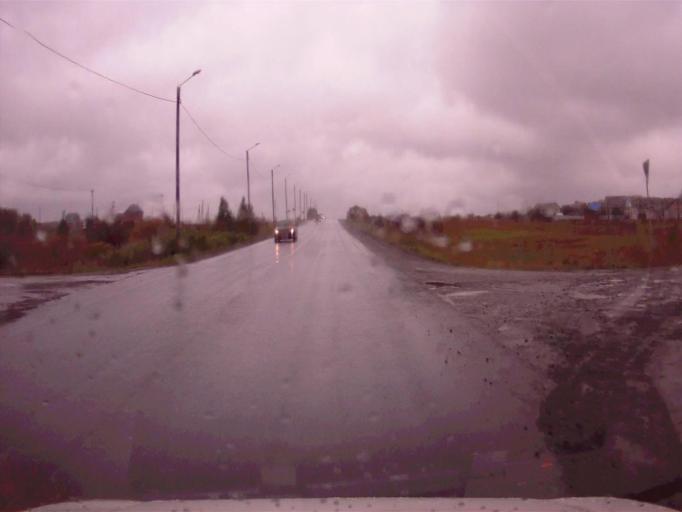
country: RU
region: Chelyabinsk
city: Argayash
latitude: 55.4774
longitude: 60.8605
